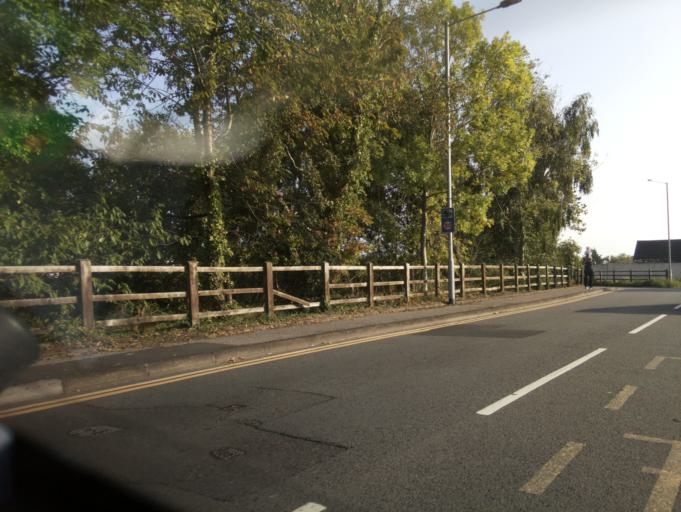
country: GB
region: Wales
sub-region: Torfaen County Borough
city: New Inn
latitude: 51.6771
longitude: -3.0209
